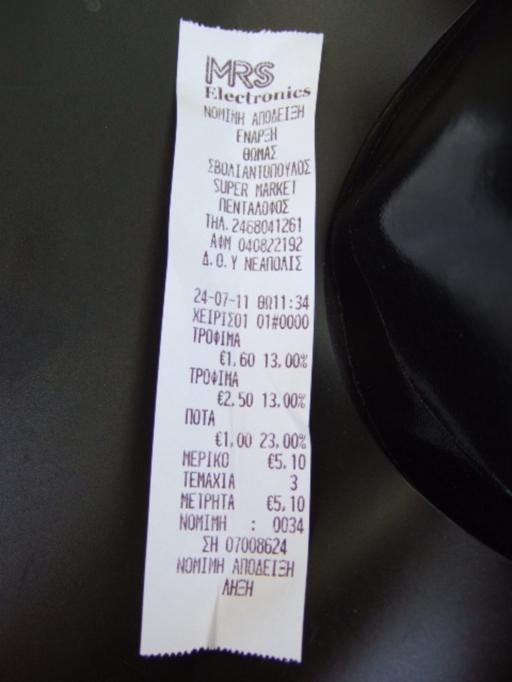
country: GR
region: West Macedonia
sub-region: Nomos Kozanis
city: Tsotili
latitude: 40.1944
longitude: 21.1411
